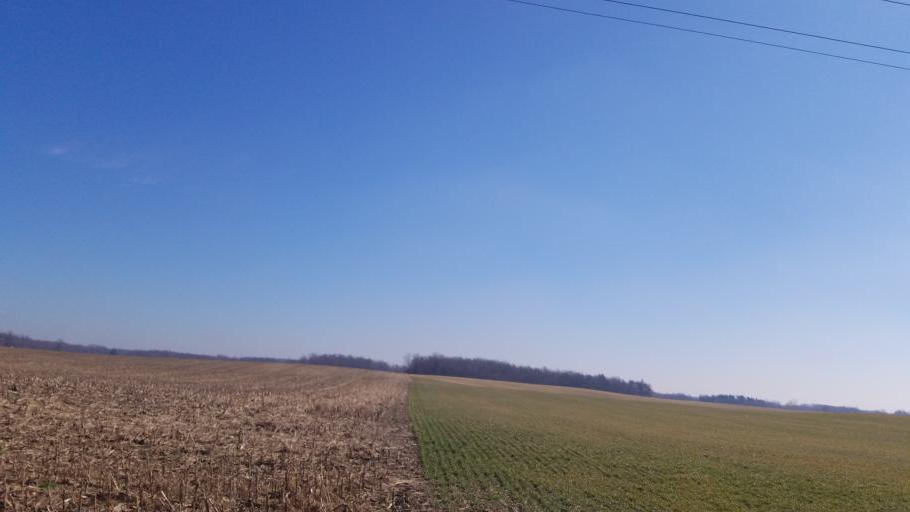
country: US
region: Ohio
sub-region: Richland County
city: Shelby
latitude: 40.9322
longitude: -82.5812
